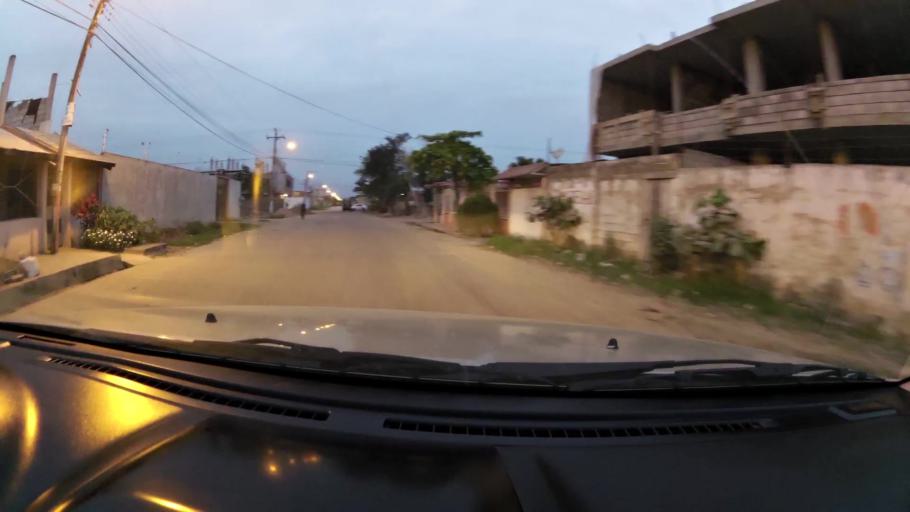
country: EC
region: El Oro
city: Machala
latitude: -3.2614
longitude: -79.9337
